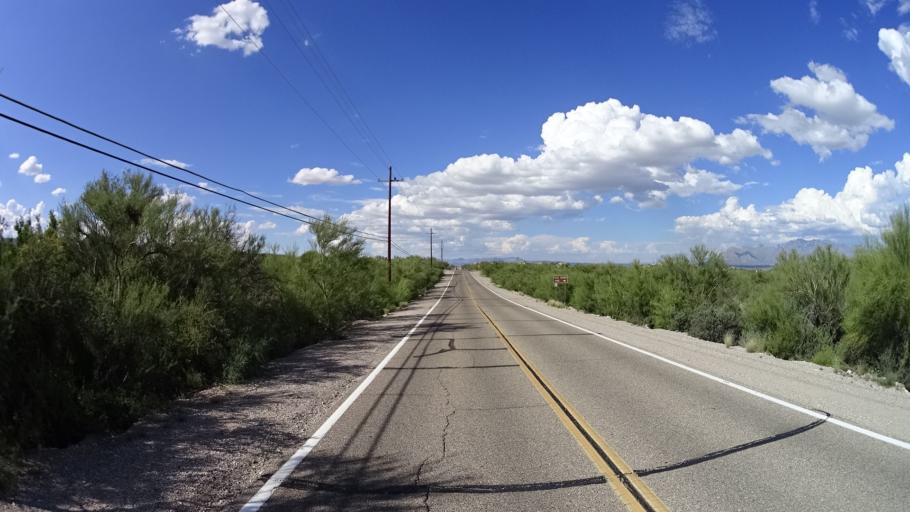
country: US
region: Arizona
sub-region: Pima County
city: Tucson Estates
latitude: 32.2393
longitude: -111.0628
